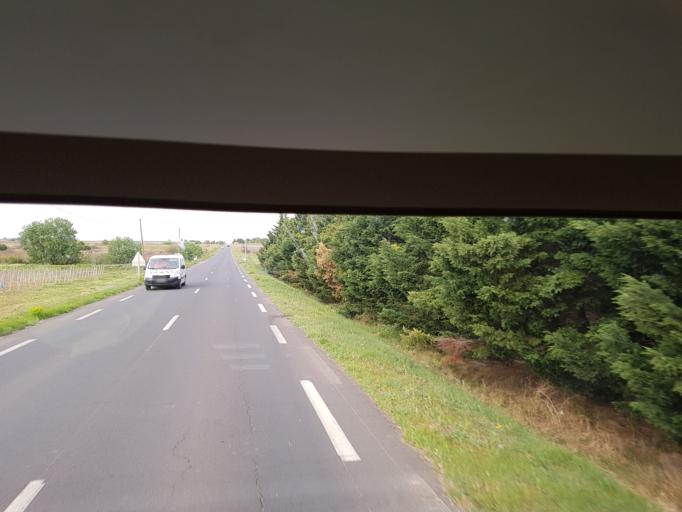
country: FR
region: Languedoc-Roussillon
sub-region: Departement de l'Herault
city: Marseillan
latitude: 43.3418
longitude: 3.5004
